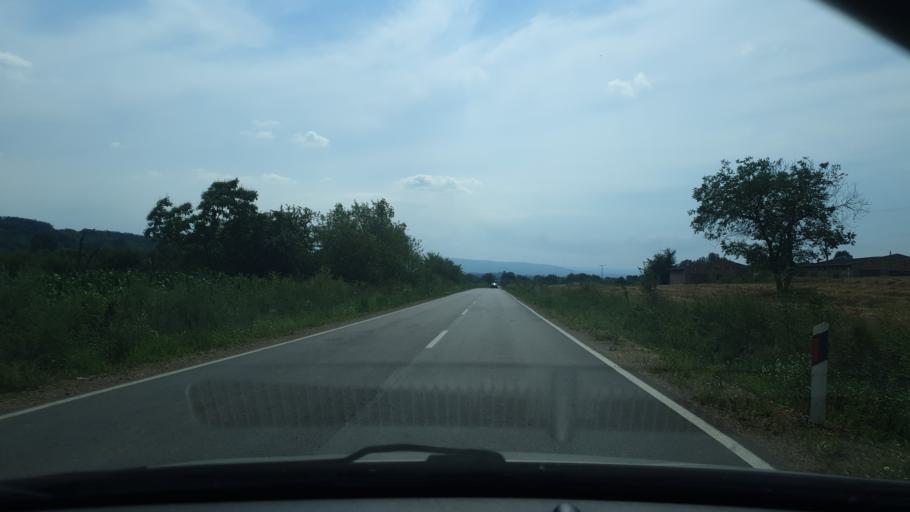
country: RS
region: Central Serbia
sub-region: Pomoravski Okrug
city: Cuprija
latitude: 43.9566
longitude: 21.4650
